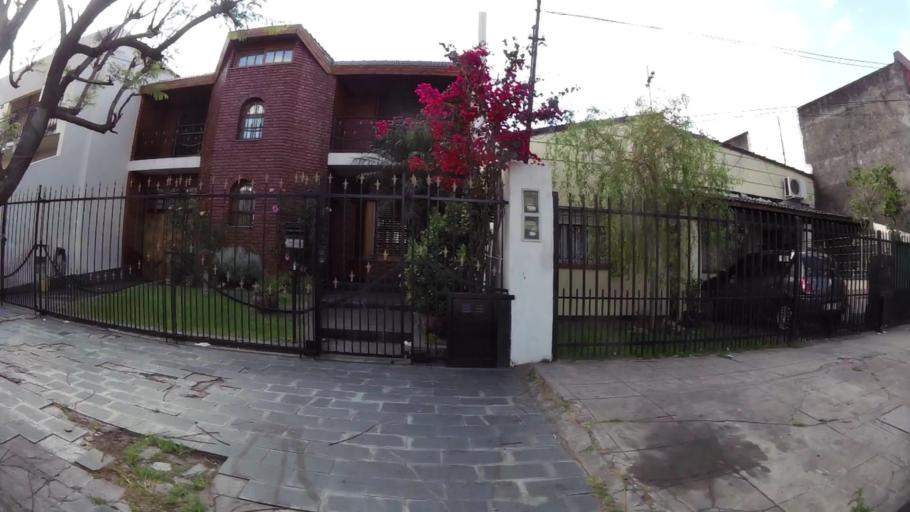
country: AR
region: Buenos Aires
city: San Justo
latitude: -34.6571
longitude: -58.5811
